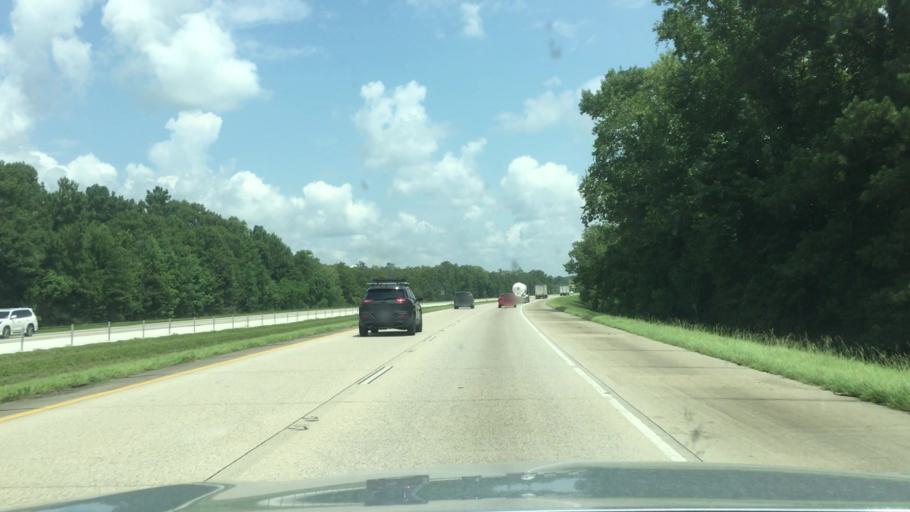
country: US
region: Louisiana
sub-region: Saint Tammany Parish
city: Pearl River
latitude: 30.3641
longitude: -89.7426
